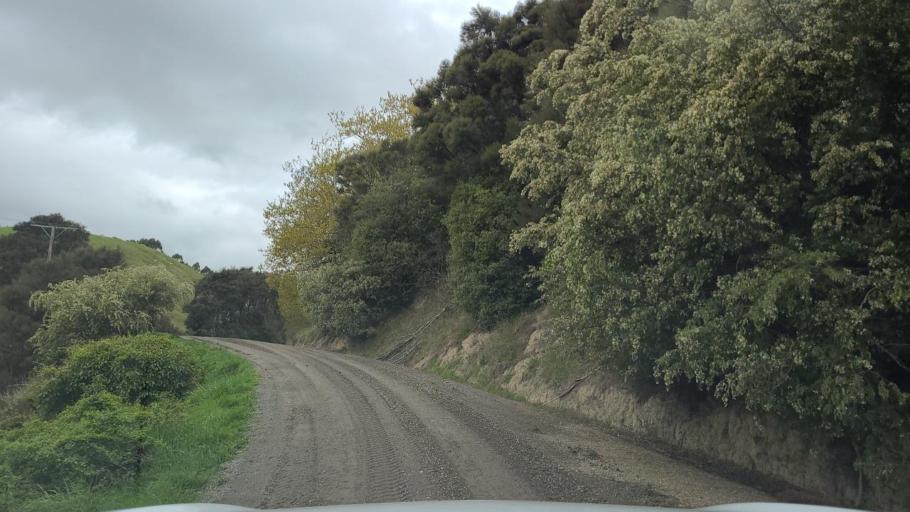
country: NZ
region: Wellington
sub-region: South Wairarapa District
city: Waipawa
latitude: -41.1973
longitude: 175.6024
